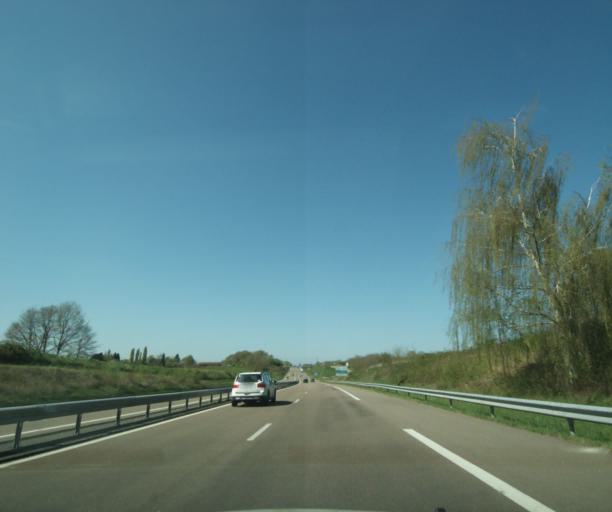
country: FR
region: Bourgogne
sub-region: Departement de la Nievre
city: Cosne-Cours-sur-Loire
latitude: 47.4202
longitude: 2.9451
